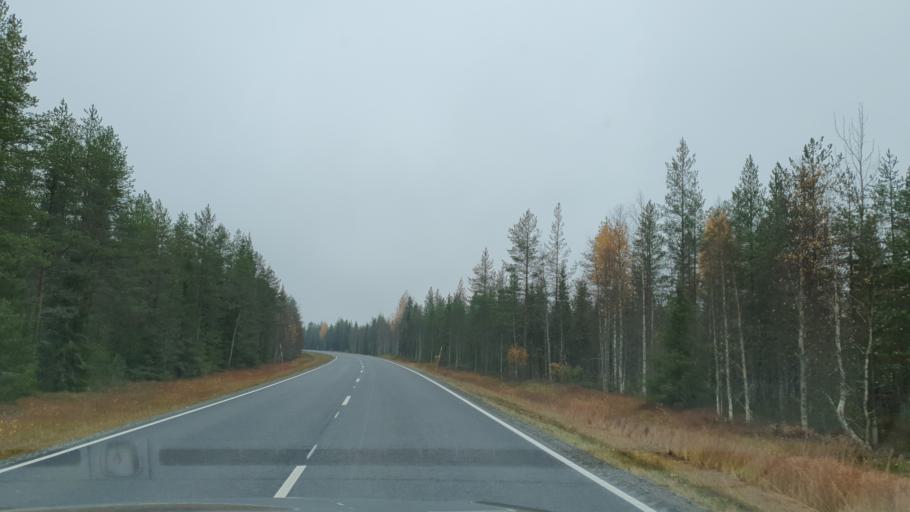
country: FI
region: Lapland
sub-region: Rovaniemi
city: Ranua
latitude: 66.1333
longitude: 26.2790
